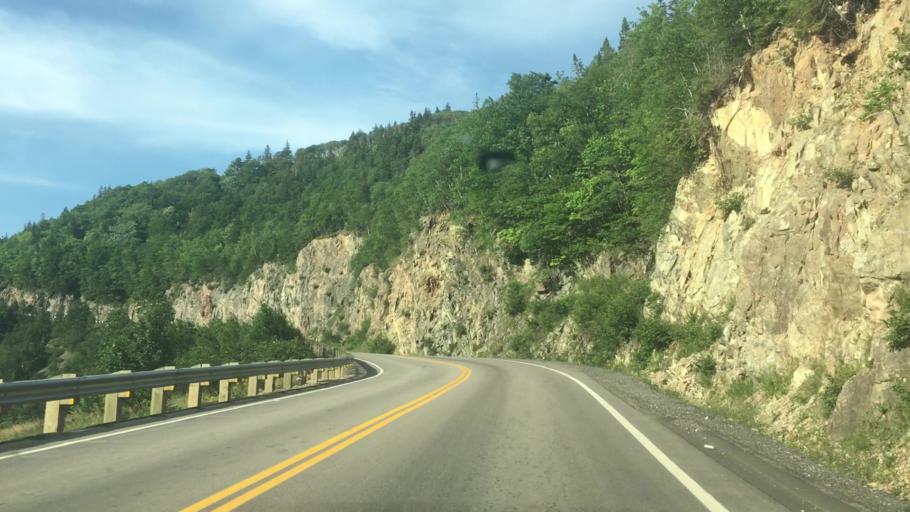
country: CA
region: Nova Scotia
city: Sydney Mines
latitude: 46.8157
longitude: -60.6513
